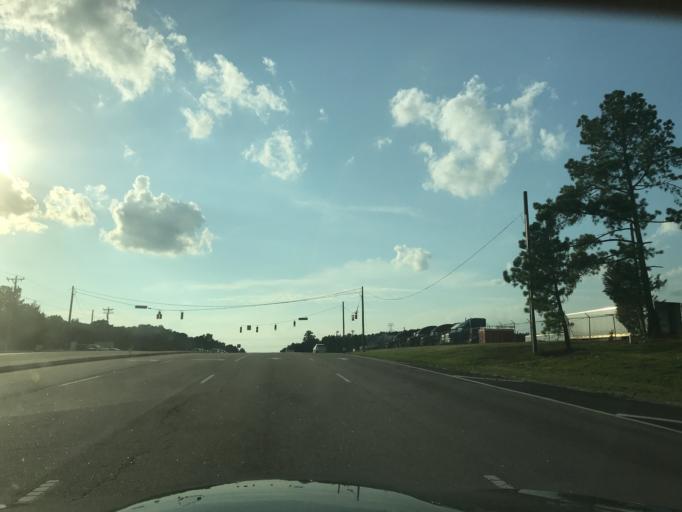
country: US
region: North Carolina
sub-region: Durham County
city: Gorman
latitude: 35.9315
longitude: -78.8083
